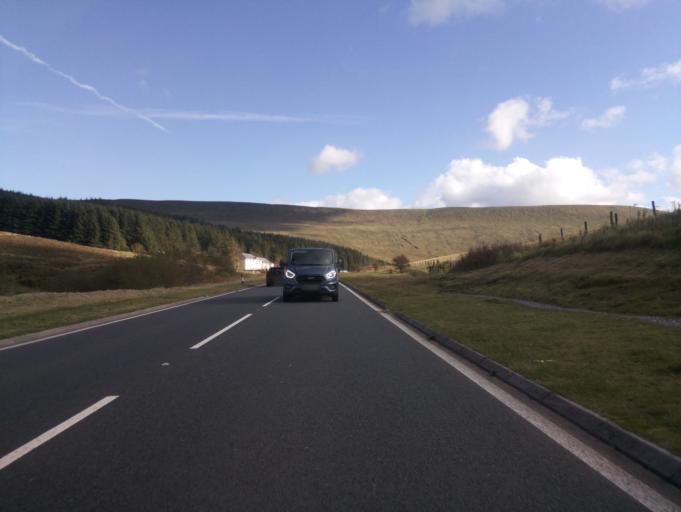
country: GB
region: Wales
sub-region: Sir Powys
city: Brecon
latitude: 51.8727
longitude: -3.4829
